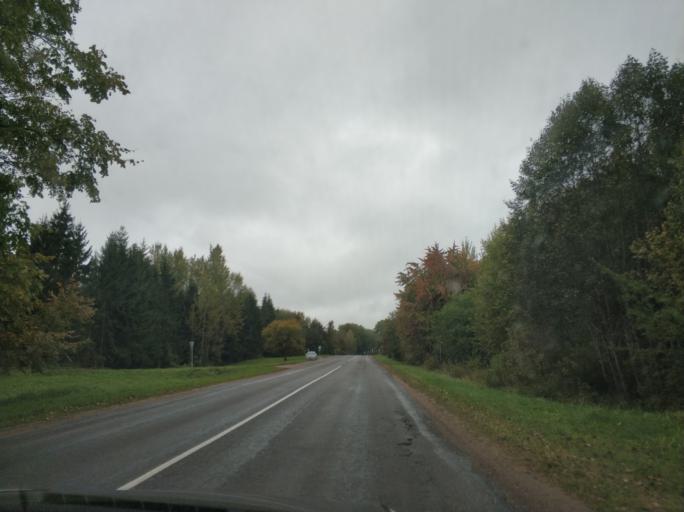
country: BY
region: Vitebsk
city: Polatsk
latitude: 55.4438
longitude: 28.9476
